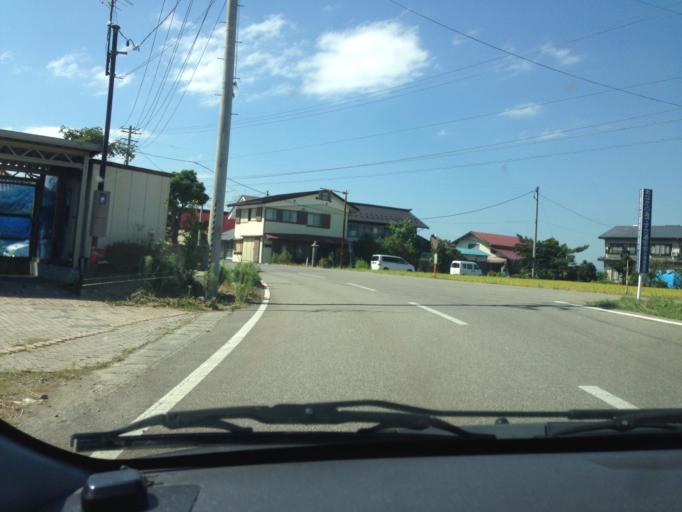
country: JP
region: Fukushima
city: Kitakata
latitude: 37.4407
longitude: 139.8578
